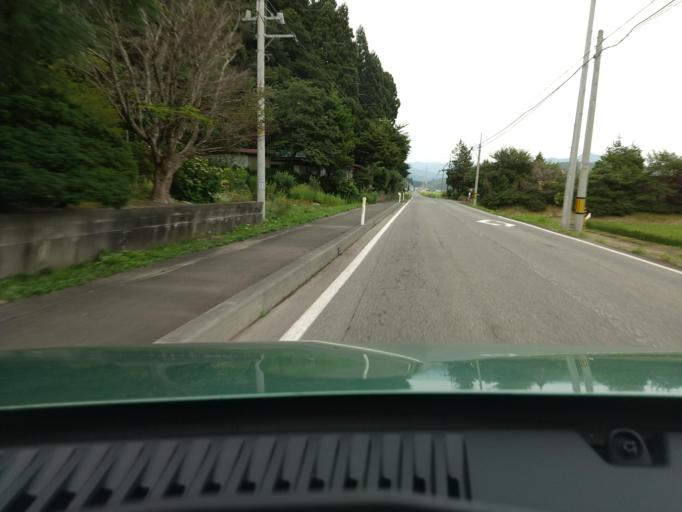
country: JP
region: Akita
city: Akita
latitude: 39.7576
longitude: 140.1495
